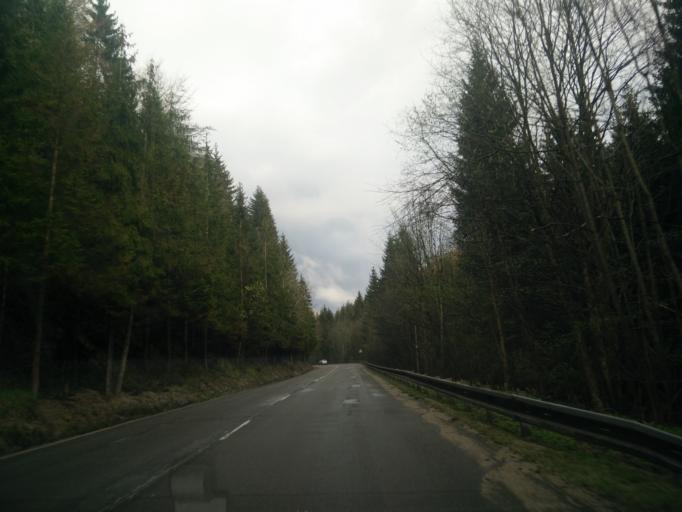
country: SK
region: Banskobystricky
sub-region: Okres Ziar nad Hronom
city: Kremnica
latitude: 48.8420
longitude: 18.9476
